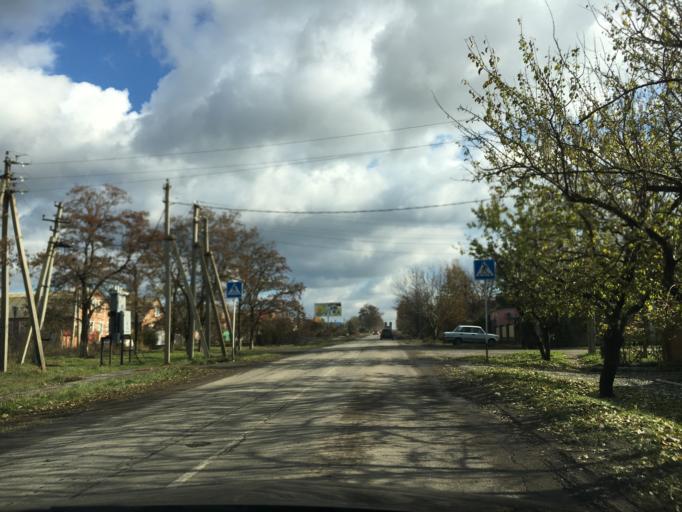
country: RU
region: Rostov
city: Matveyev Kurgan
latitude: 47.5634
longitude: 38.8792
